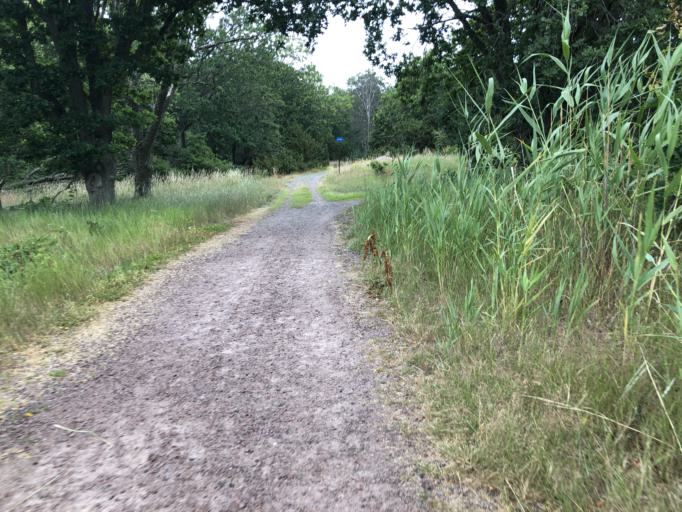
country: SE
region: Kalmar
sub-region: Kalmar Kommun
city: Kalmar
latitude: 56.6395
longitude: 16.3218
